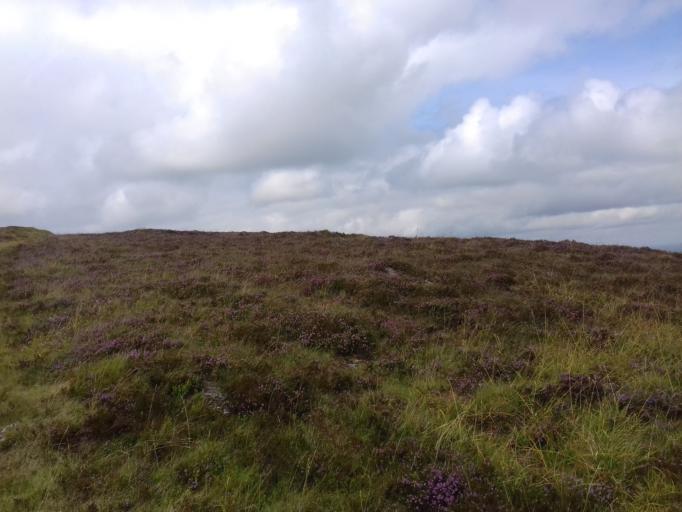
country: IE
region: Leinster
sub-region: Loch Garman
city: Bunclody
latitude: 52.6380
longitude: -6.7978
